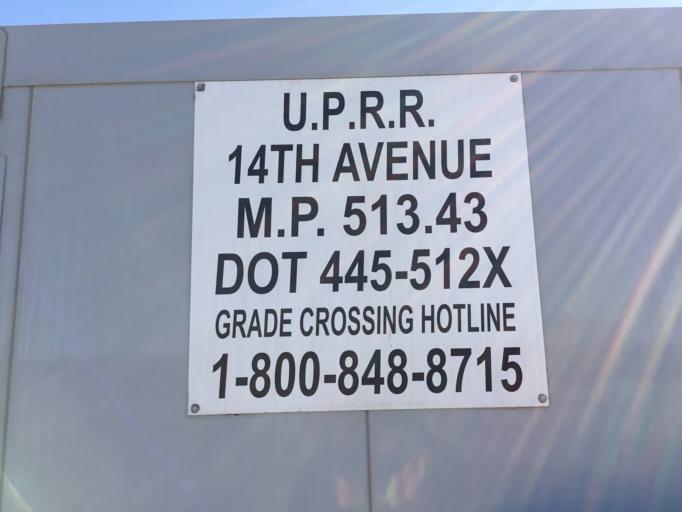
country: US
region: Kansas
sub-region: McPherson County
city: McPherson
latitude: 38.3339
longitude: -97.6671
